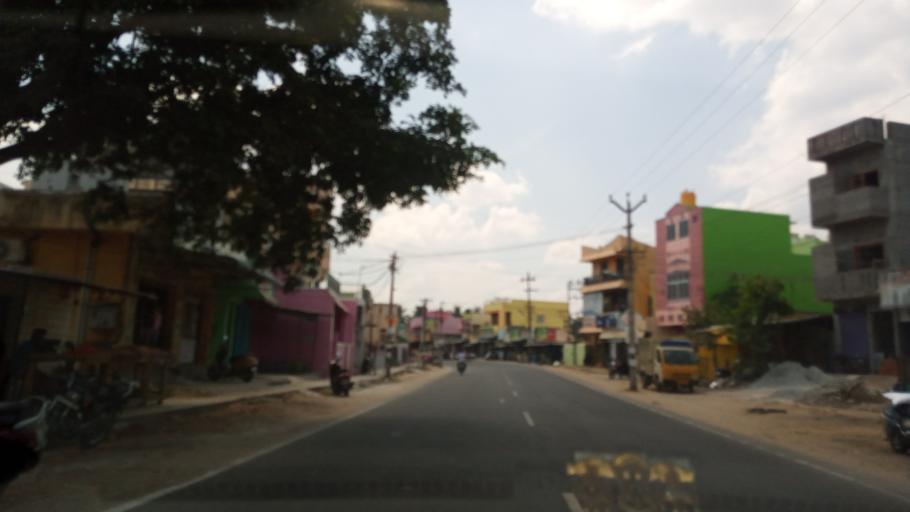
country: IN
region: Tamil Nadu
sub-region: Vellore
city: Walajapet
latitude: 12.9245
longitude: 79.3709
